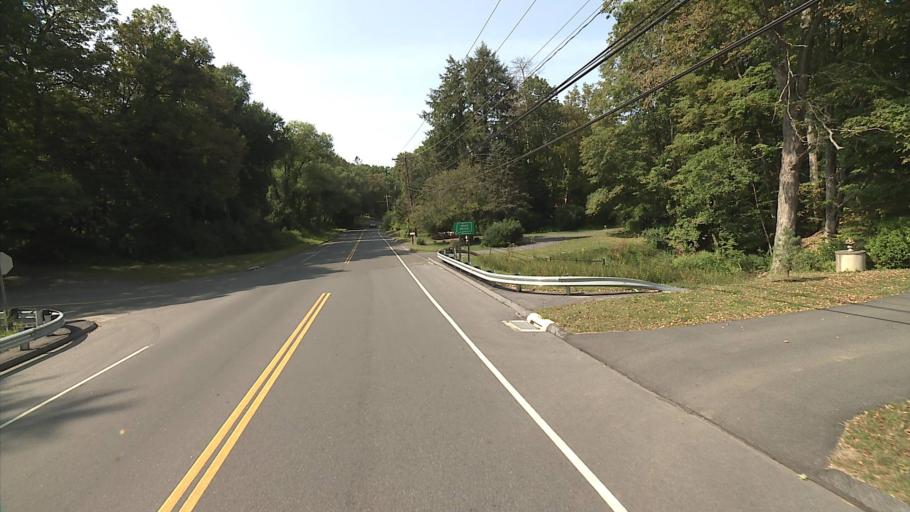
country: US
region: Connecticut
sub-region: New Haven County
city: Heritage Village
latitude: 41.4626
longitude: -73.2425
